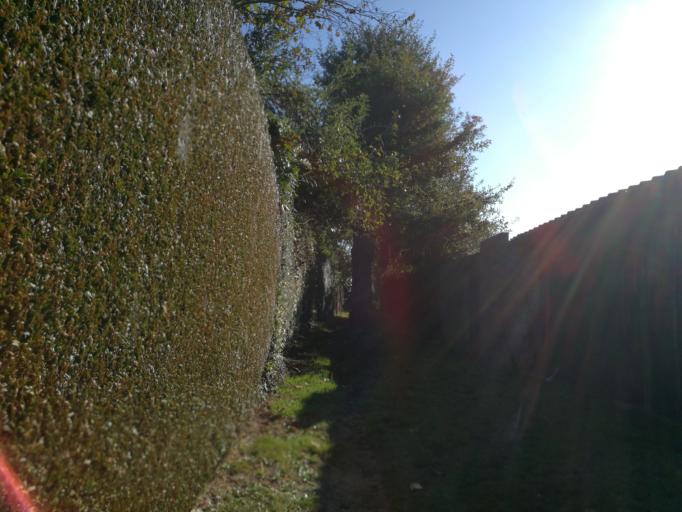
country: FR
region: Brittany
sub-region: Departement d'Ille-et-Vilaine
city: Bedee
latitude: 48.1759
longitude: -1.9413
